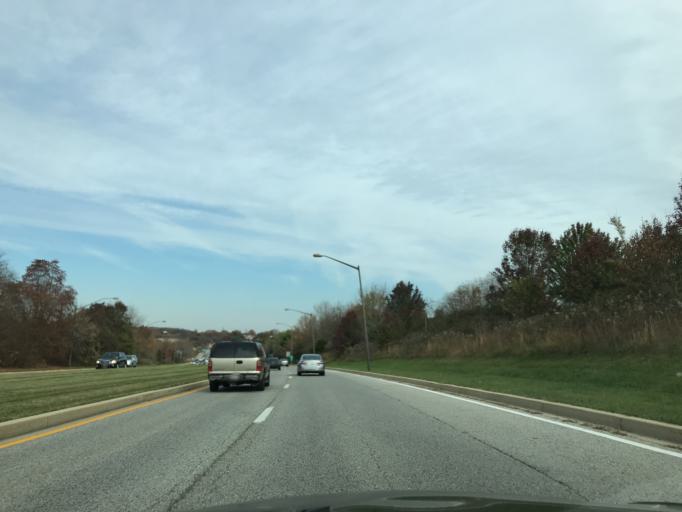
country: US
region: Maryland
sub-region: Anne Arundel County
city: Jessup
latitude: 39.1928
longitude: -76.8099
